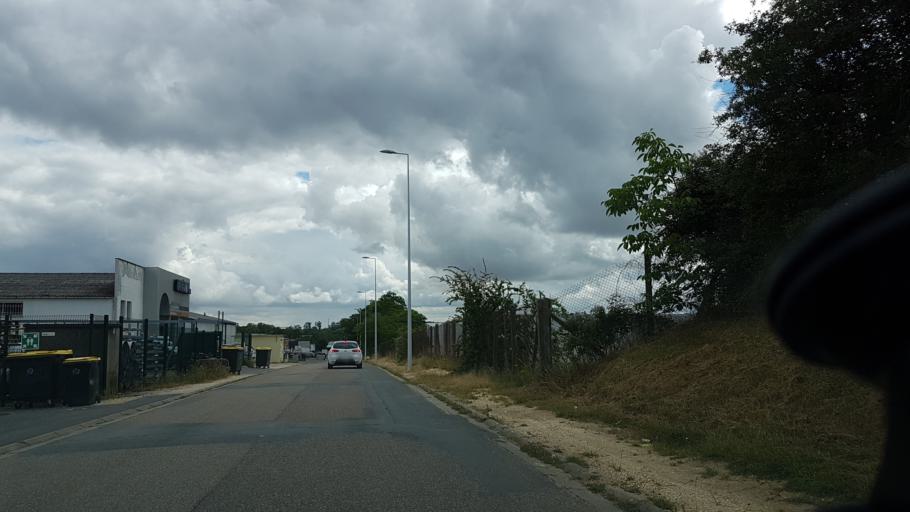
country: FR
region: Centre
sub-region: Departement du Cher
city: Bourges
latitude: 47.1038
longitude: 2.3849
